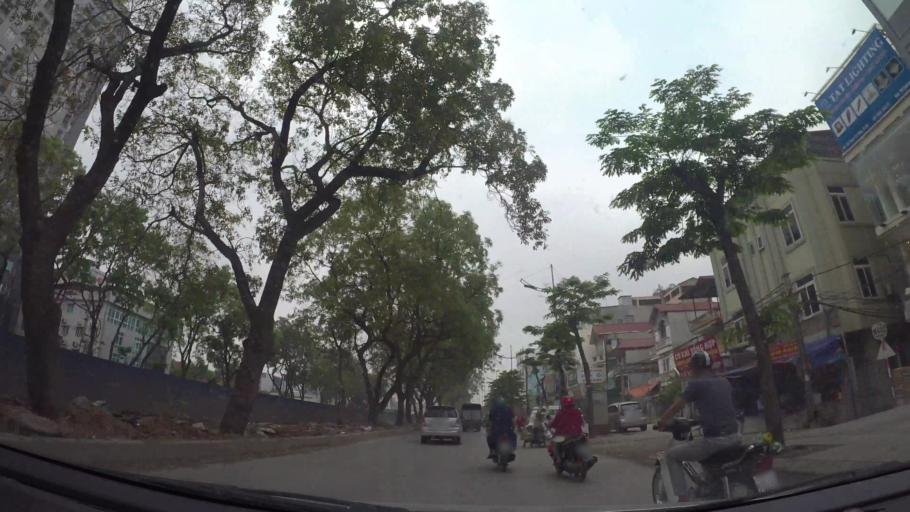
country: VN
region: Ha Noi
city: Cau Dien
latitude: 21.0437
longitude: 105.7808
